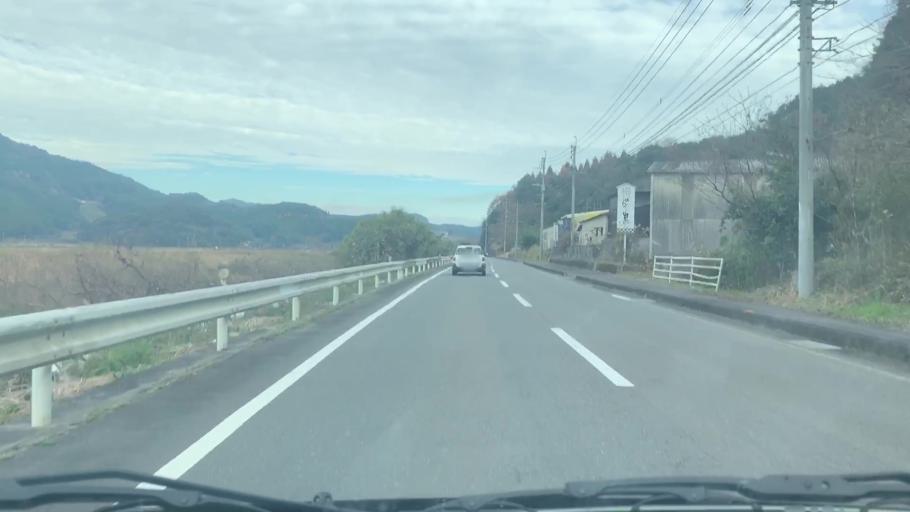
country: JP
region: Saga Prefecture
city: Imaricho-ko
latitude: 33.2738
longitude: 129.9648
